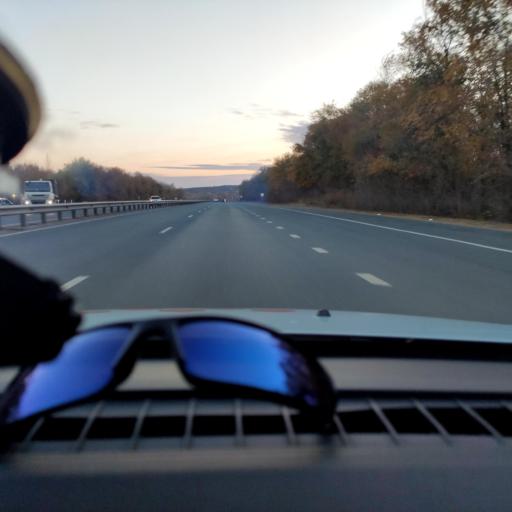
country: RU
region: Samara
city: Novokuybyshevsk
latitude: 53.0523
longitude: 50.0124
